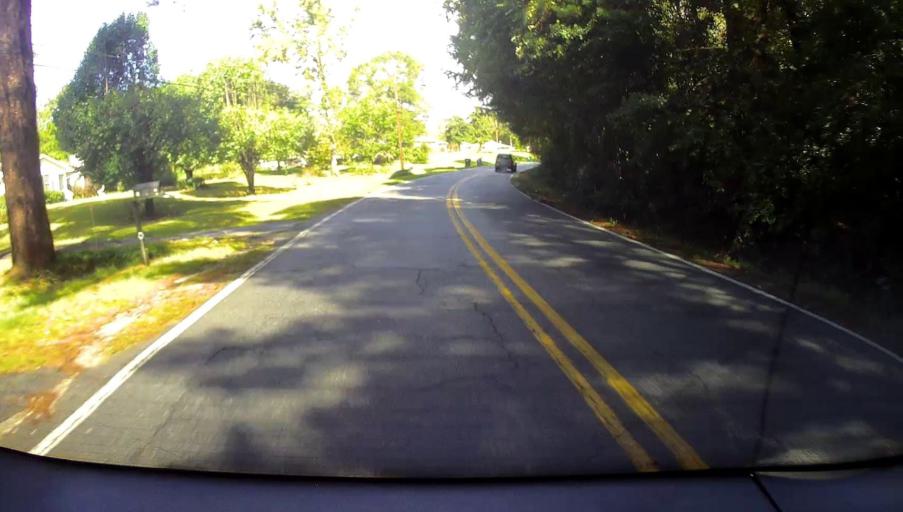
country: US
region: Georgia
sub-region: Bibb County
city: Macon
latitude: 32.9150
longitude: -83.7204
